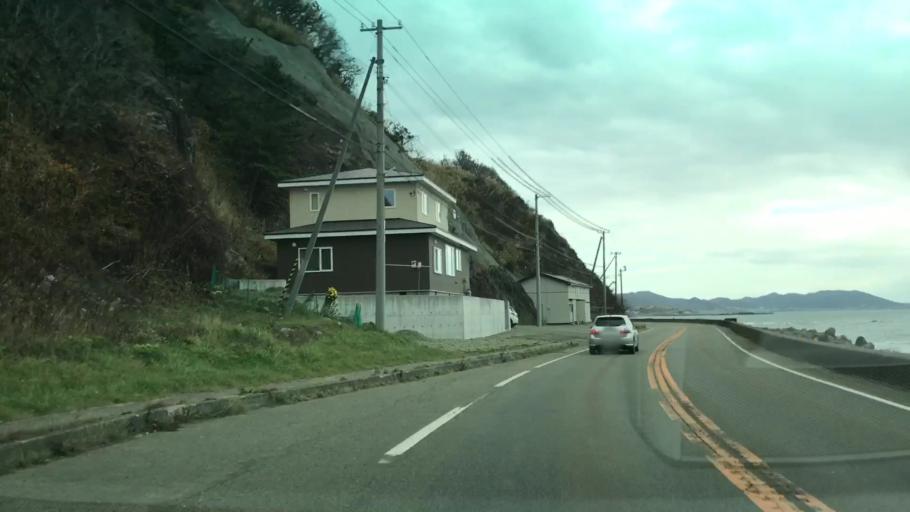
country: JP
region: Hokkaido
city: Shizunai-furukawacho
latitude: 42.0564
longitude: 143.0795
